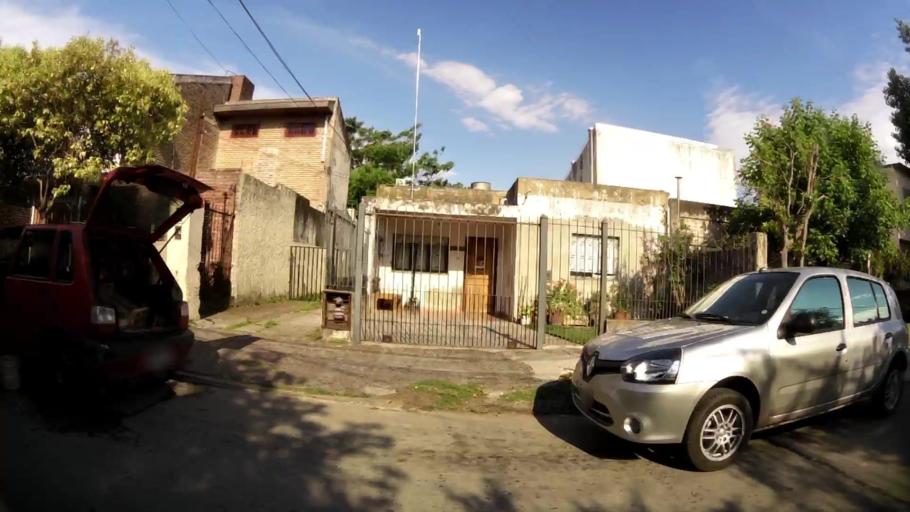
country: AR
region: Buenos Aires
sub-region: Partido de Merlo
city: Merlo
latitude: -34.6598
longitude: -58.7237
